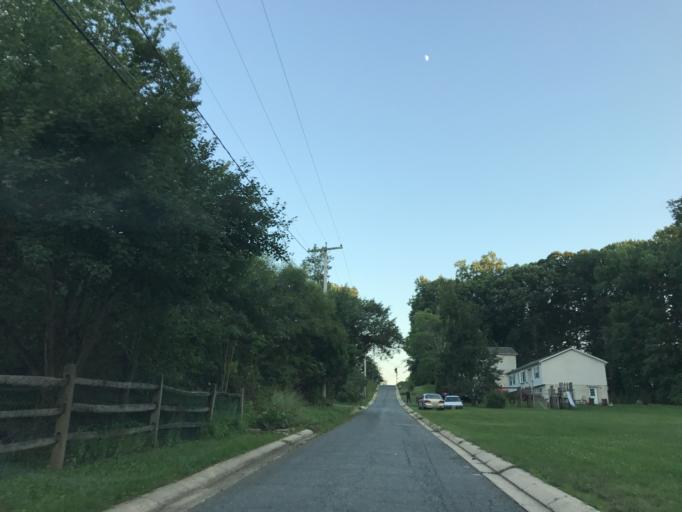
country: US
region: Maryland
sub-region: Harford County
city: Joppatowne
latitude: 39.4339
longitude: -76.3711
